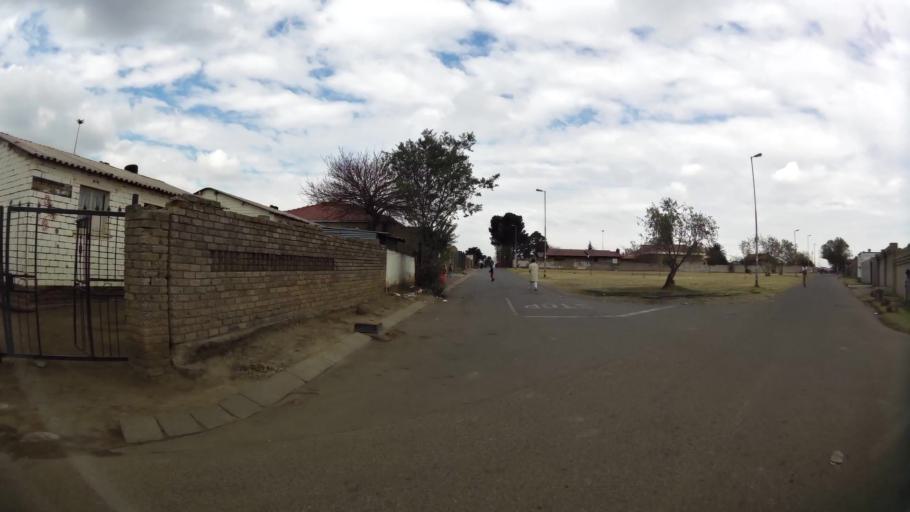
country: ZA
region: Gauteng
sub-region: City of Johannesburg Metropolitan Municipality
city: Soweto
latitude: -26.2697
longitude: 27.8633
